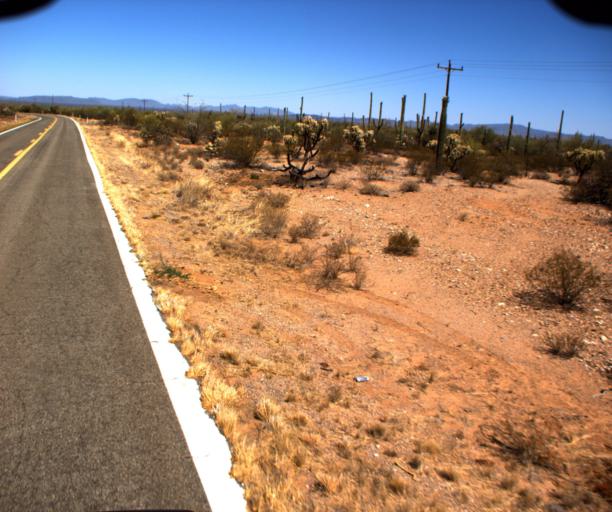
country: US
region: Arizona
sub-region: Pima County
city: Sells
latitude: 32.1808
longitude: -112.2784
